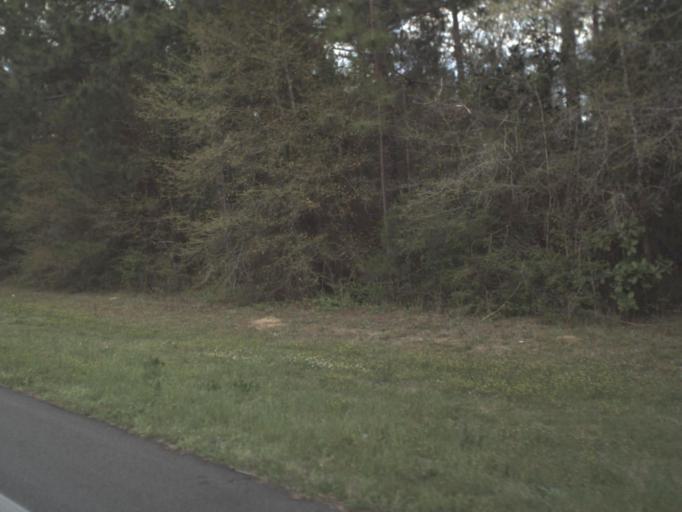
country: US
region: Florida
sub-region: Okaloosa County
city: Crestview
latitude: 30.8934
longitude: -86.5069
